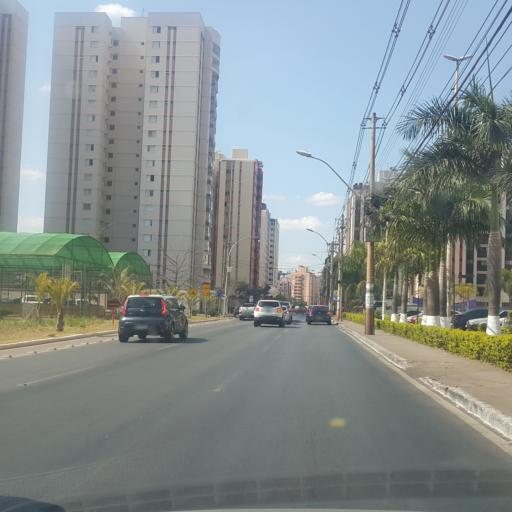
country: BR
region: Federal District
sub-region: Brasilia
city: Brasilia
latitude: -15.8391
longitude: -48.0188
